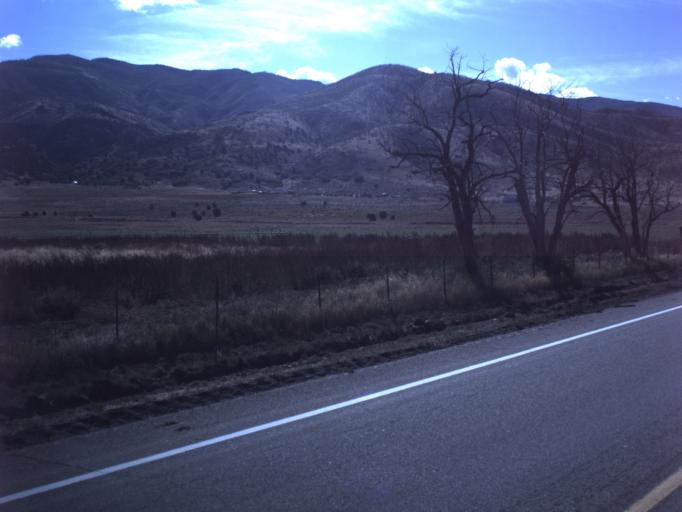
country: US
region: Utah
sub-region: Juab County
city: Nephi
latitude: 39.5424
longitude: -111.8638
